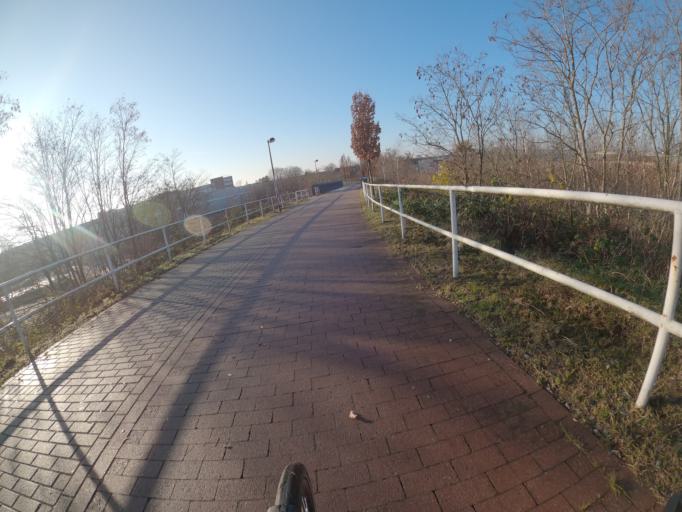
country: DE
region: Lower Saxony
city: Lilienthal
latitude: 53.0514
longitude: 8.9054
